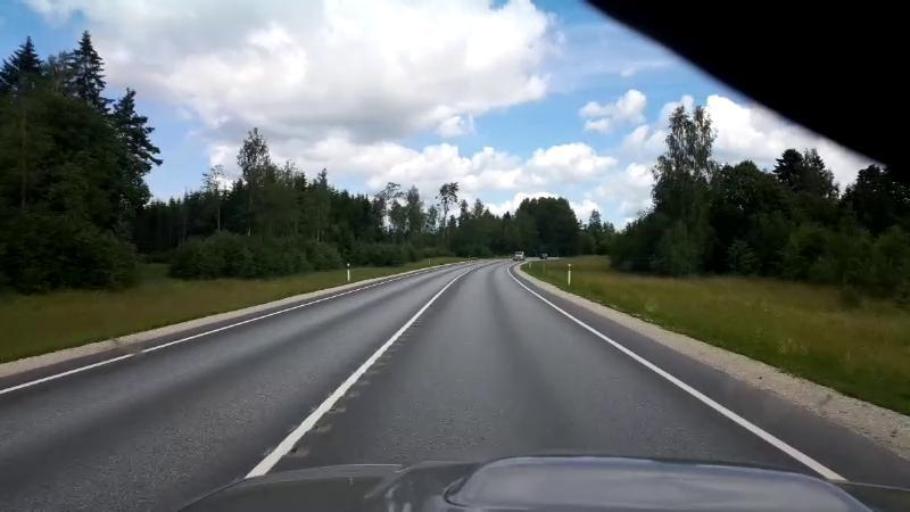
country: EE
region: Laeaene-Virumaa
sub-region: Tapa vald
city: Tapa
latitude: 59.2802
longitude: 26.0408
